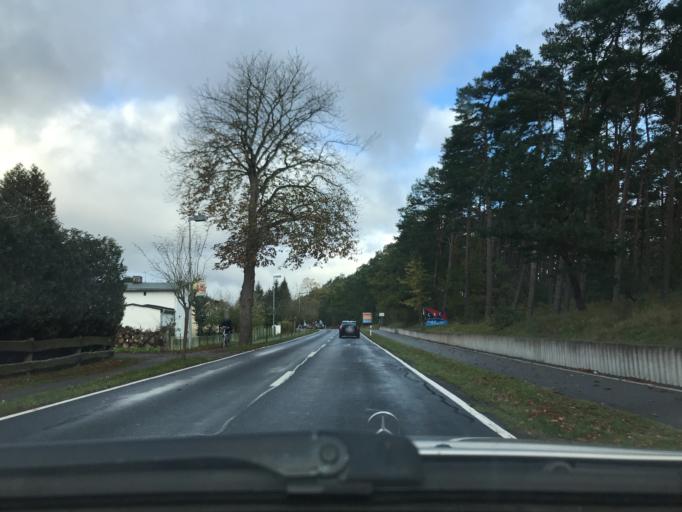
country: DE
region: Mecklenburg-Vorpommern
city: Karlshagen
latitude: 54.1064
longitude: 13.8442
